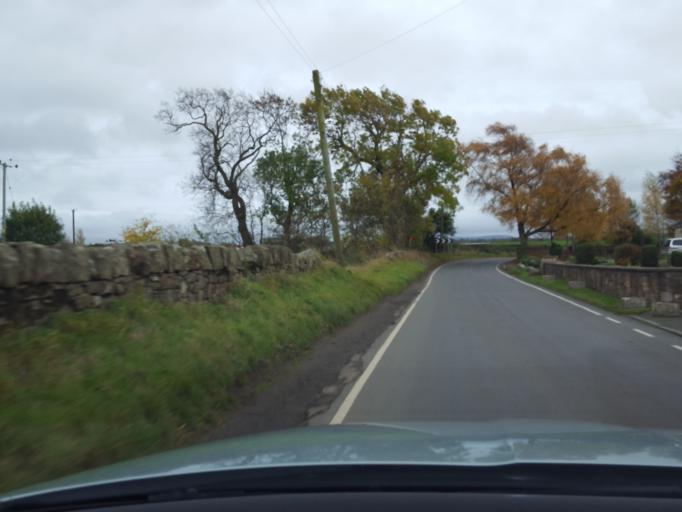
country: GB
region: Scotland
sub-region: West Lothian
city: East Calder
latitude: 55.9014
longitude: -3.4451
